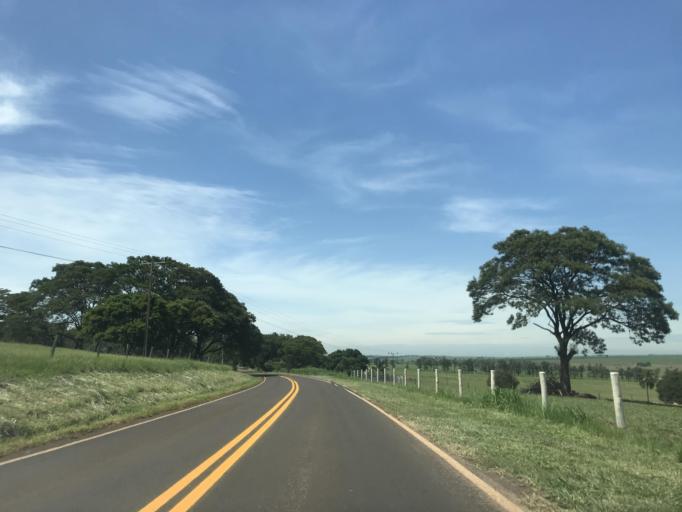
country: BR
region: Parana
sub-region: Terra Rica
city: Terra Rica
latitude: -22.7820
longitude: -52.6574
